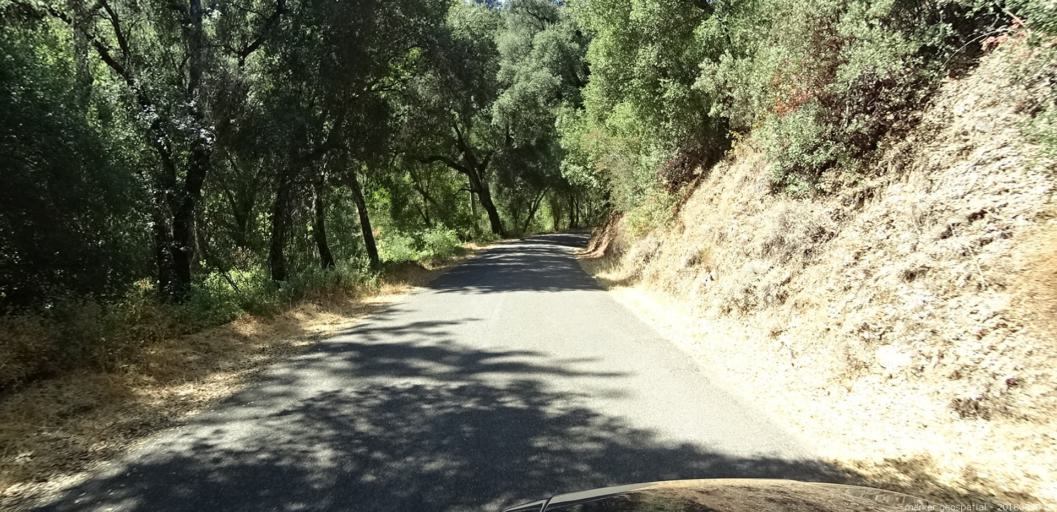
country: US
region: California
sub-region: Monterey County
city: King City
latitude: 36.0082
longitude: -121.4019
